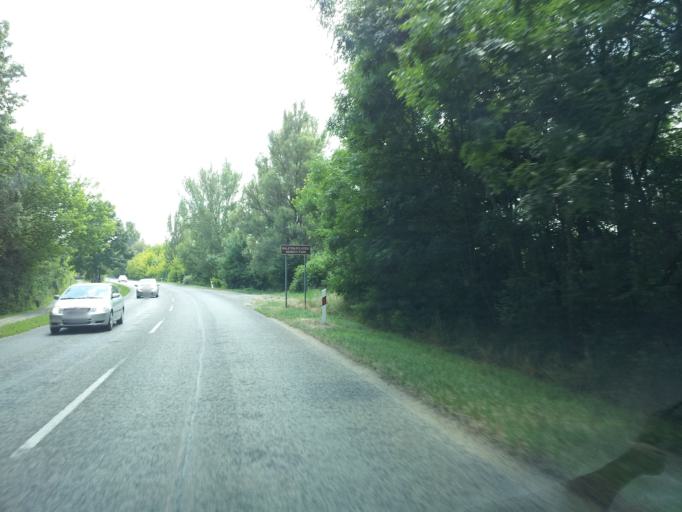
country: HU
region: Veszprem
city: Balatonfured
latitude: 46.9347
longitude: 17.8594
